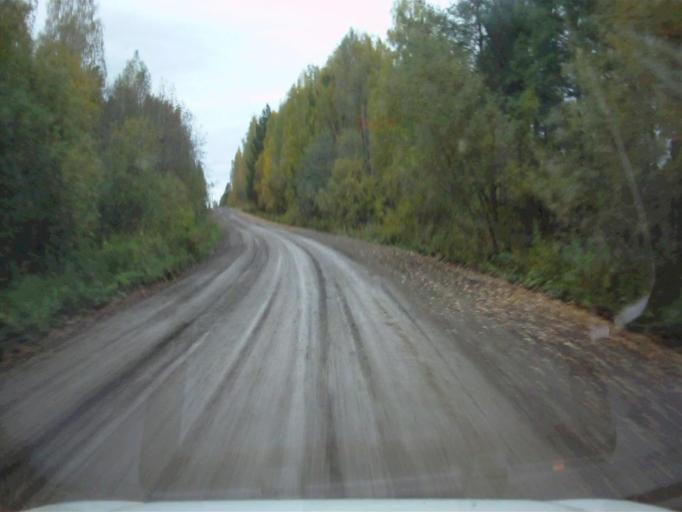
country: RU
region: Chelyabinsk
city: Nyazepetrovsk
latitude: 56.1049
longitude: 59.3847
